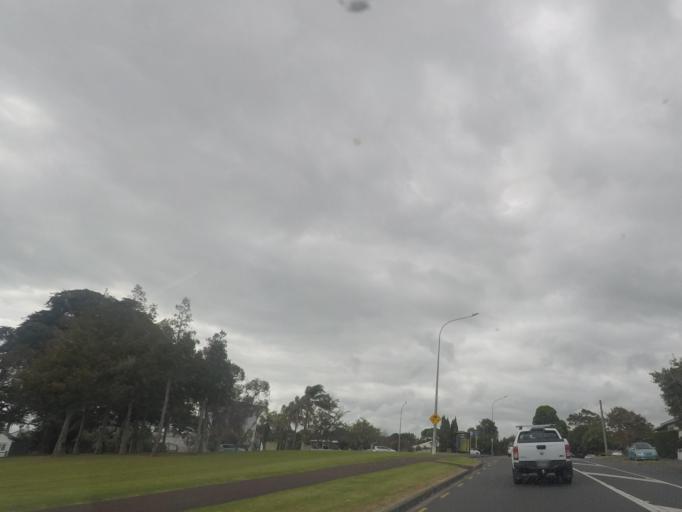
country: NZ
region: Auckland
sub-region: Auckland
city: Tamaki
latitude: -36.8655
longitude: 174.8441
